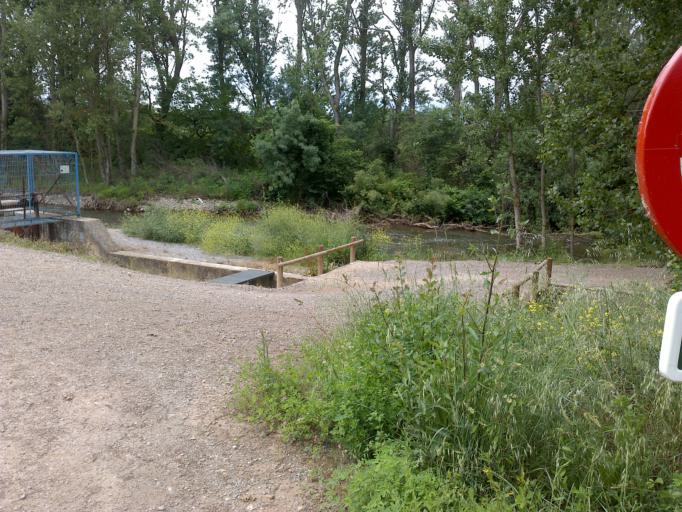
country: ES
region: La Rioja
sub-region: Provincia de La Rioja
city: Albelda de Iregua
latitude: 42.3767
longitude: -2.4662
